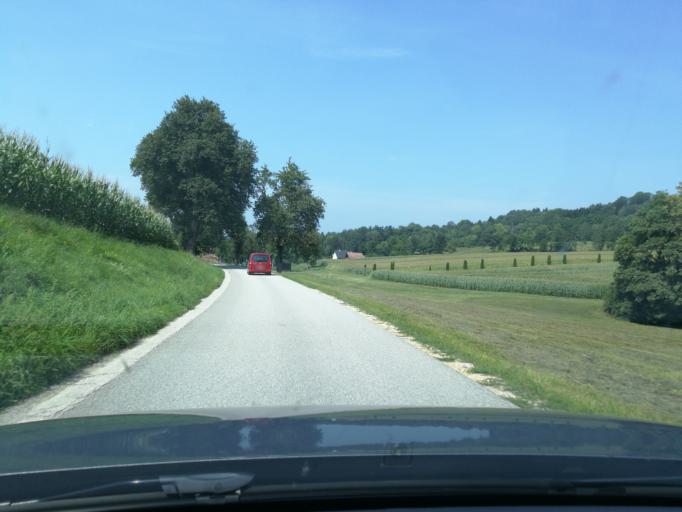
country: DE
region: Bavaria
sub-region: Lower Bavaria
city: Obernzell
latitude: 48.3695
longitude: 13.6620
